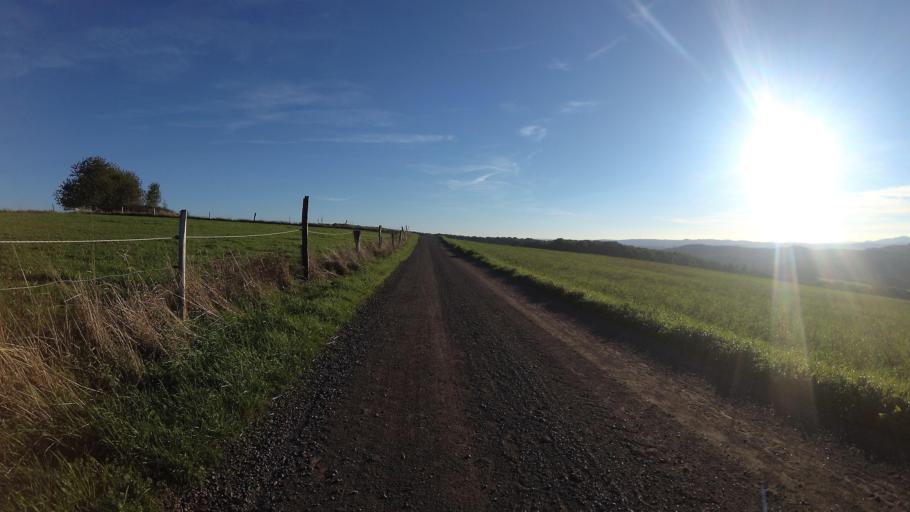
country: DE
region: Saarland
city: Sankt Wendel
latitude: 49.4988
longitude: 7.2053
